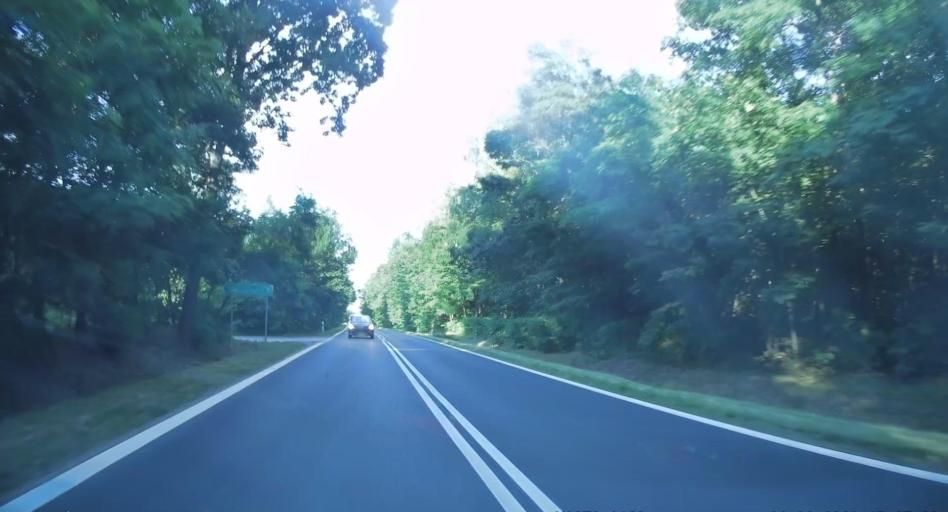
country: PL
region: Lodz Voivodeship
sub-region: Powiat rawski
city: Rawa Mazowiecka
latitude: 51.7810
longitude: 20.3116
